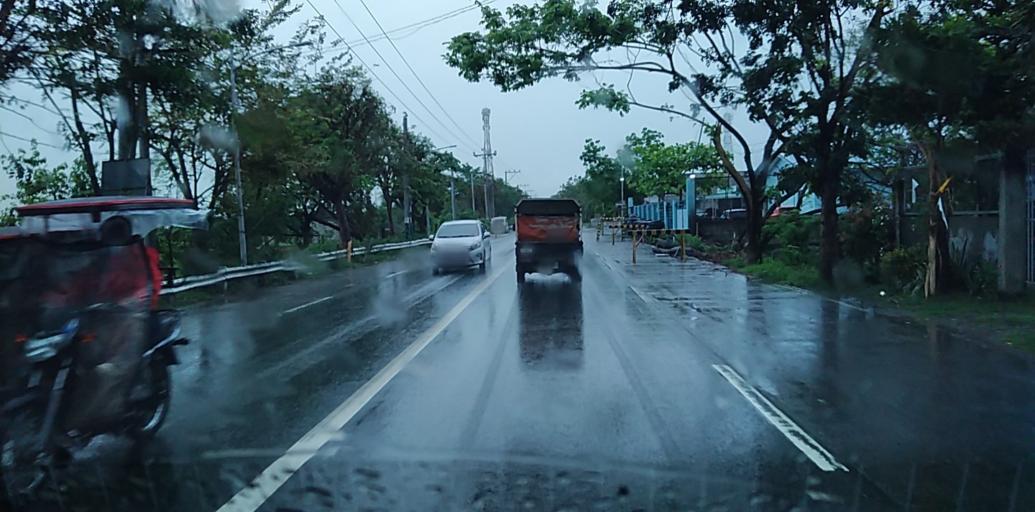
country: PH
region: Central Luzon
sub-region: Province of Bulacan
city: Bulualto
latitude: 15.2150
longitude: 120.9550
